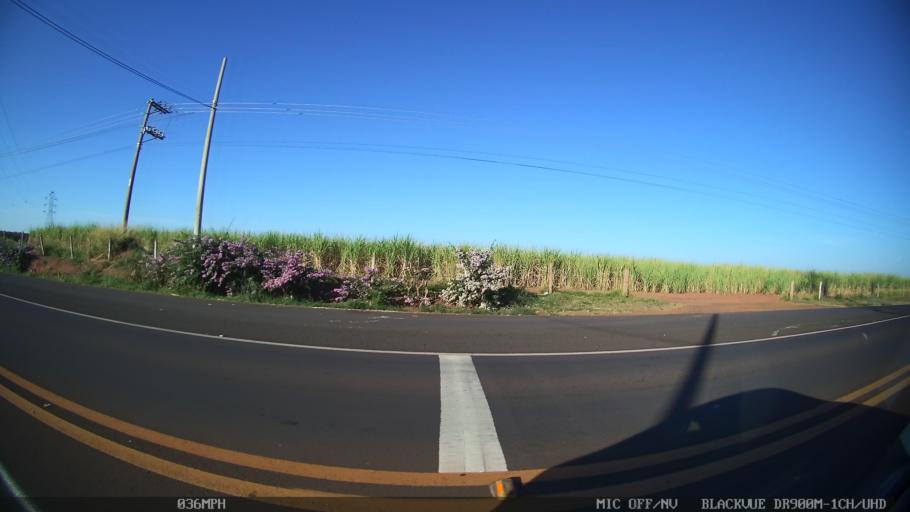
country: BR
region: Sao Paulo
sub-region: Guapiacu
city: Guapiacu
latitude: -20.7760
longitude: -49.2249
